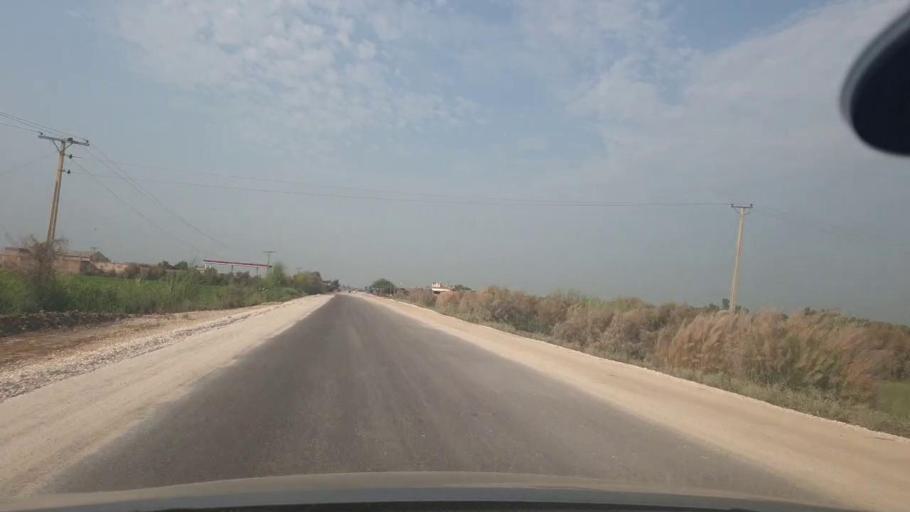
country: PK
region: Sindh
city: Jacobabad
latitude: 28.1399
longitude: 68.3411
